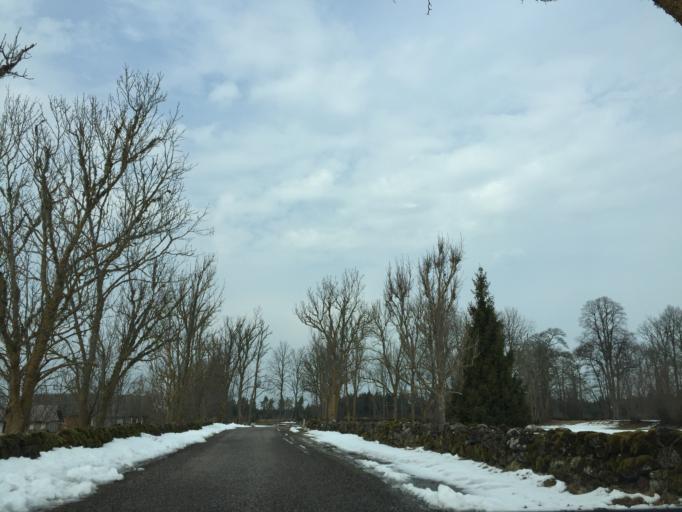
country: EE
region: Saare
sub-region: Kuressaare linn
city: Kuressaare
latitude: 58.4209
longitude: 22.1512
